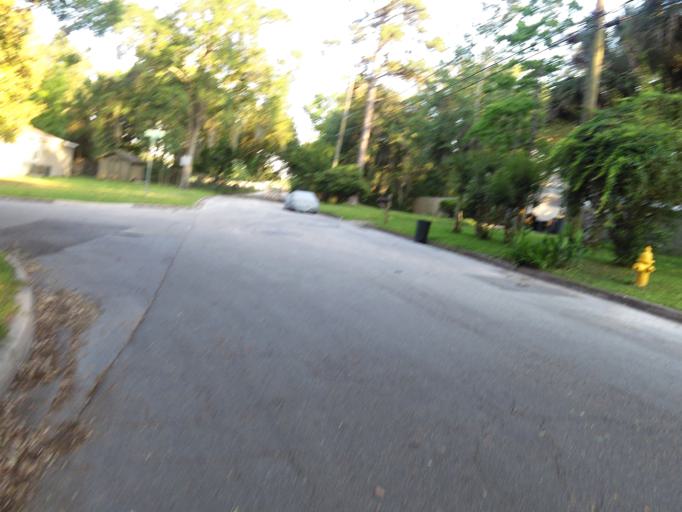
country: US
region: Florida
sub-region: Duval County
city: Jacksonville
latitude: 30.3036
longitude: -81.6468
